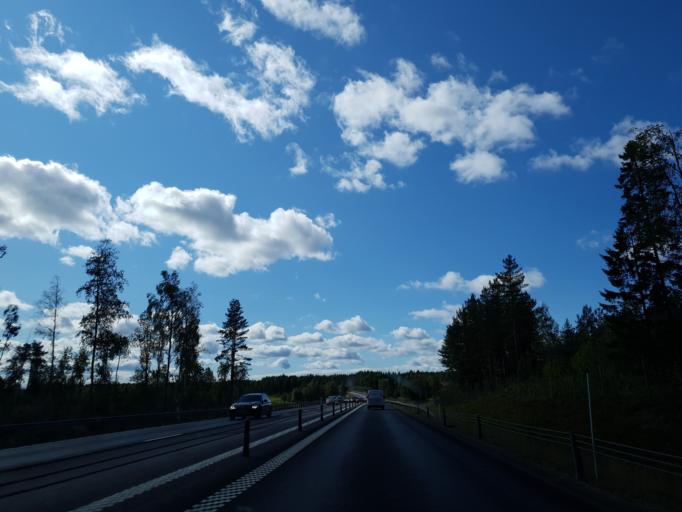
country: SE
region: Vaesterbotten
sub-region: Nordmalings Kommun
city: Nordmaling
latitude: 63.5004
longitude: 19.3342
